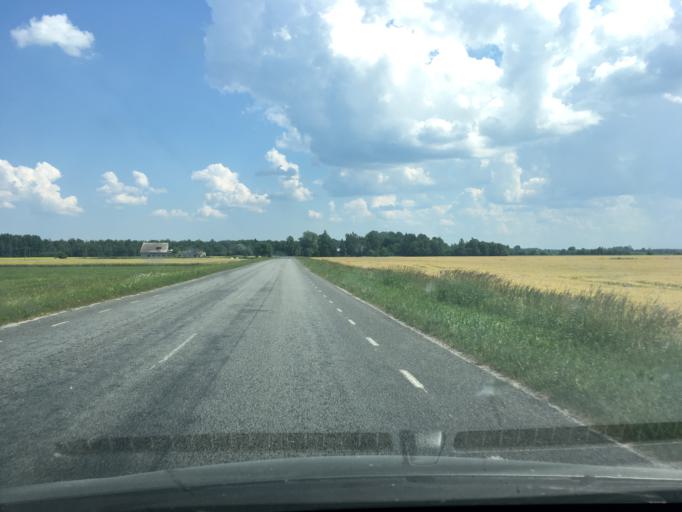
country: EE
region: Raplamaa
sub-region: Maerjamaa vald
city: Marjamaa
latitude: 58.7317
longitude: 24.2944
